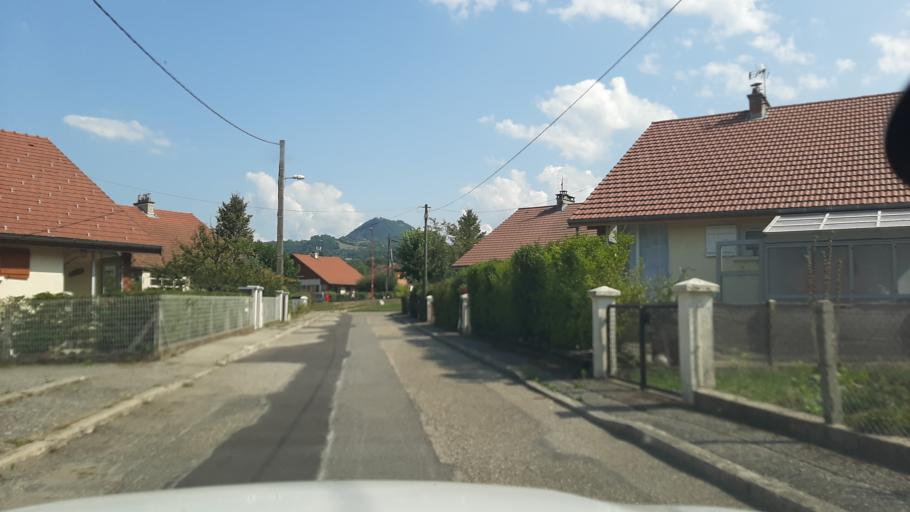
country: FR
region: Rhone-Alpes
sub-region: Departement de la Savoie
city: La Rochette
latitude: 45.4508
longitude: 6.1116
